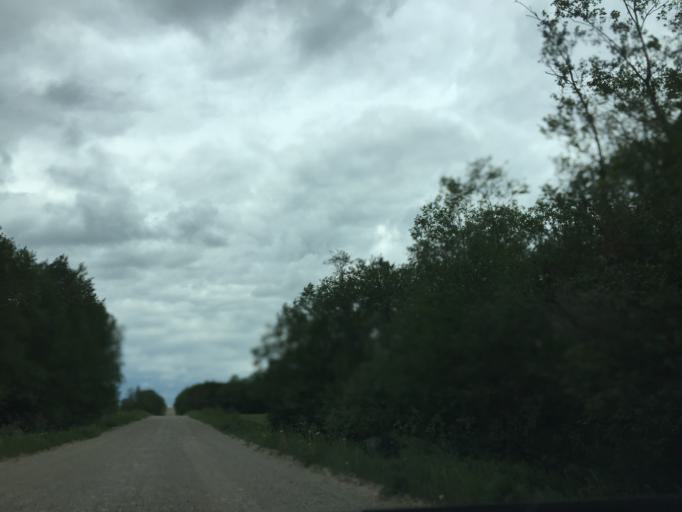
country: LV
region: Dagda
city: Dagda
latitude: 55.9986
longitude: 27.6091
